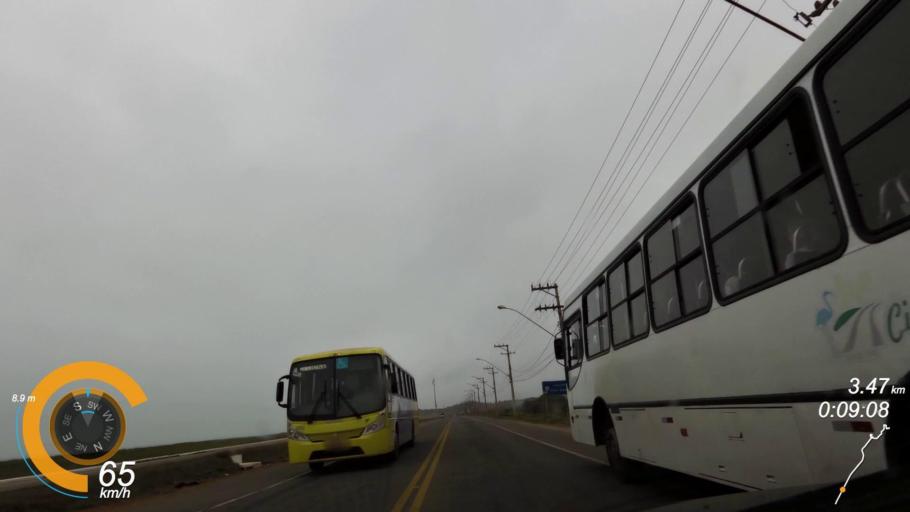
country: BR
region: Espirito Santo
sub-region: Guarapari
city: Guarapari
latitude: -20.6893
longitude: -40.5103
